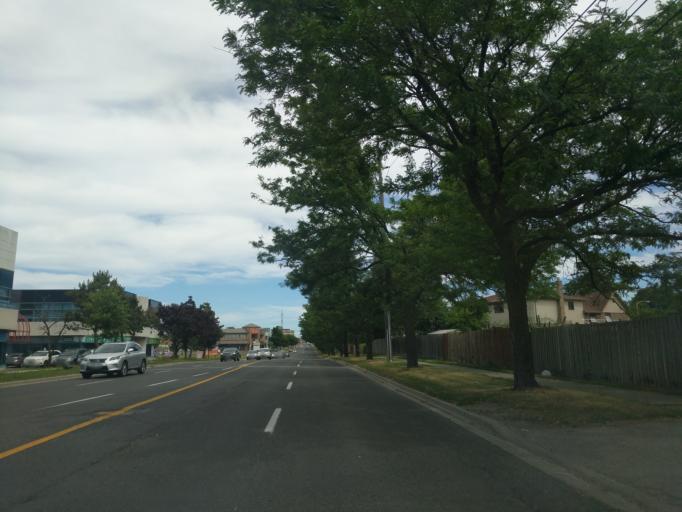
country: CA
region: Ontario
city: Scarborough
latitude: 43.8075
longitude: -79.2890
